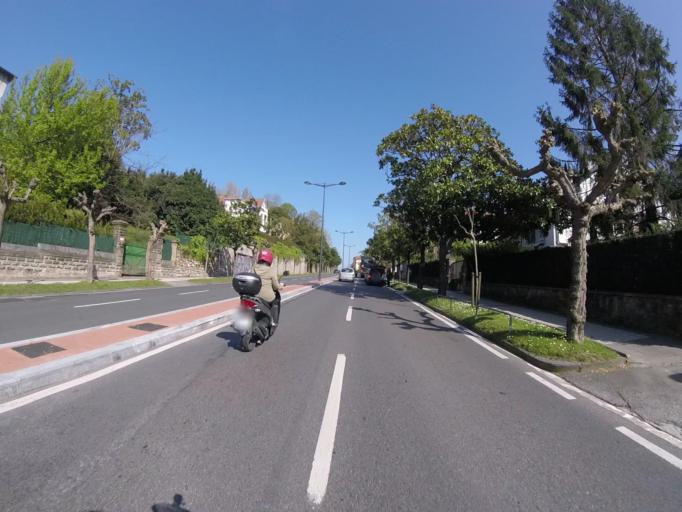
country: ES
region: Basque Country
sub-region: Provincia de Guipuzcoa
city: San Sebastian
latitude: 43.3214
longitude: -1.9527
